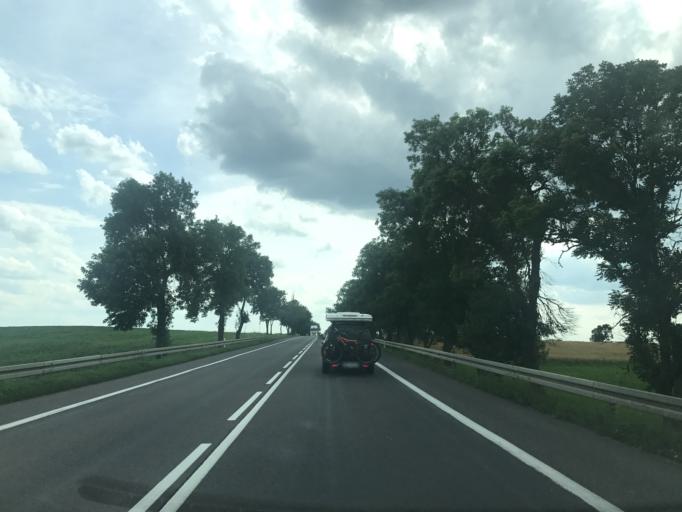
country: PL
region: Masovian Voivodeship
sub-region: Powiat mlawski
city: Wisniewo
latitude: 53.0464
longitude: 20.3427
